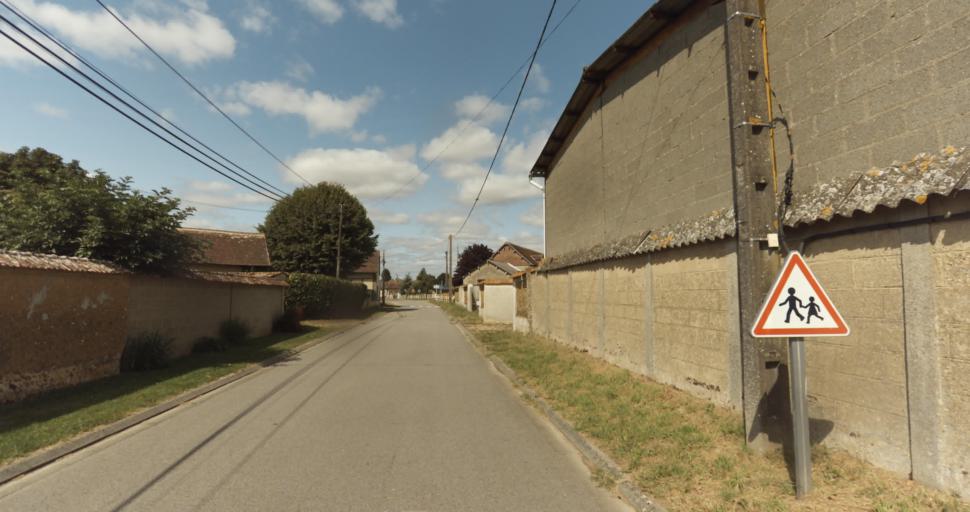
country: FR
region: Haute-Normandie
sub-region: Departement de l'Eure
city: Nonancourt
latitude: 48.8382
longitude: 1.1656
